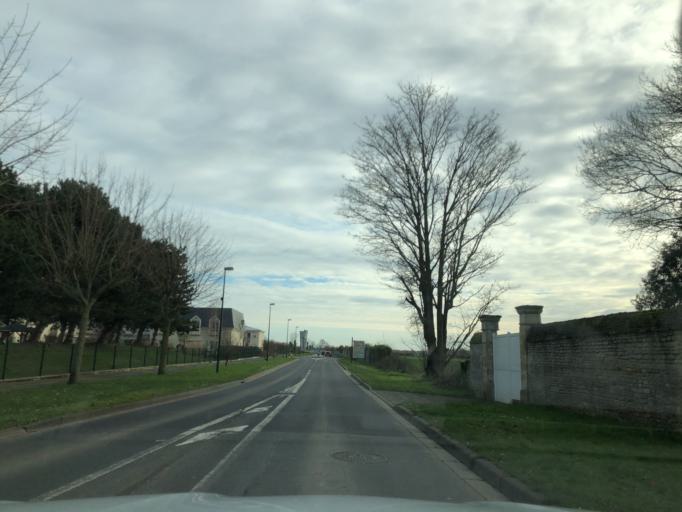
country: FR
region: Lower Normandy
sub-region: Departement du Calvados
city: Beuville
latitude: 49.2419
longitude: -0.3212
